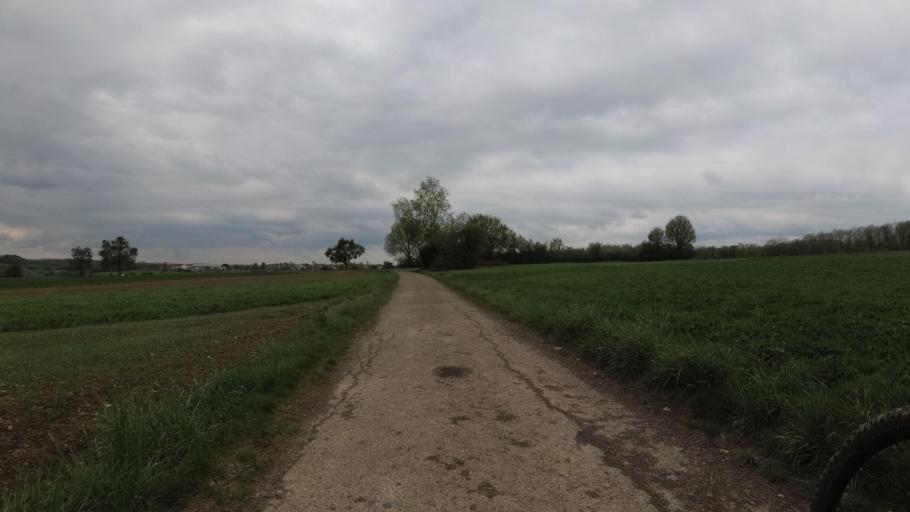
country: DE
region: Saarland
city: Merzig
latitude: 49.4136
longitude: 6.5634
